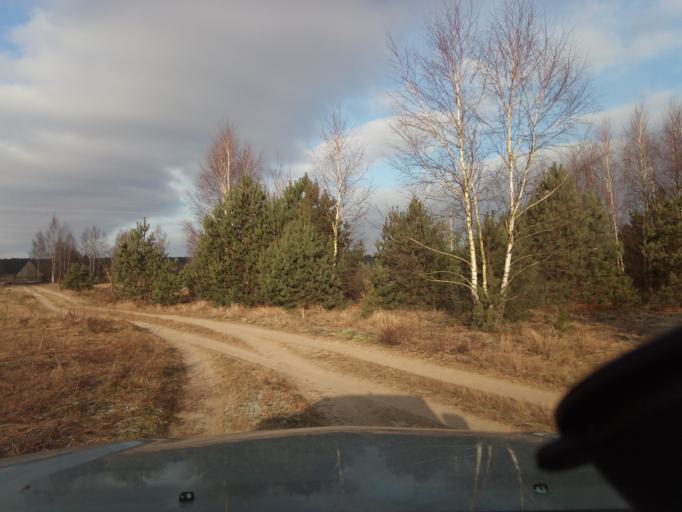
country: LT
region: Alytaus apskritis
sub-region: Alytaus rajonas
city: Daugai
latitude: 54.1138
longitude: 24.2382
